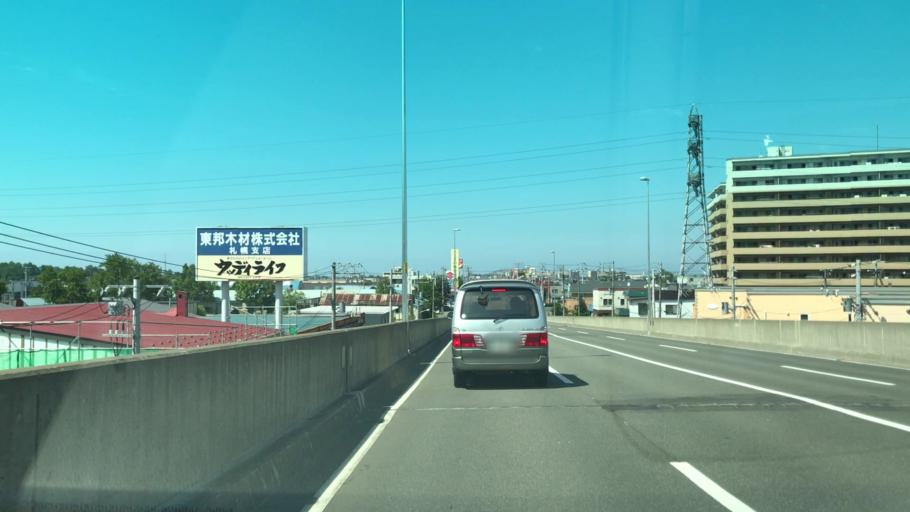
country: JP
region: Hokkaido
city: Sapporo
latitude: 43.1255
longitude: 141.2359
